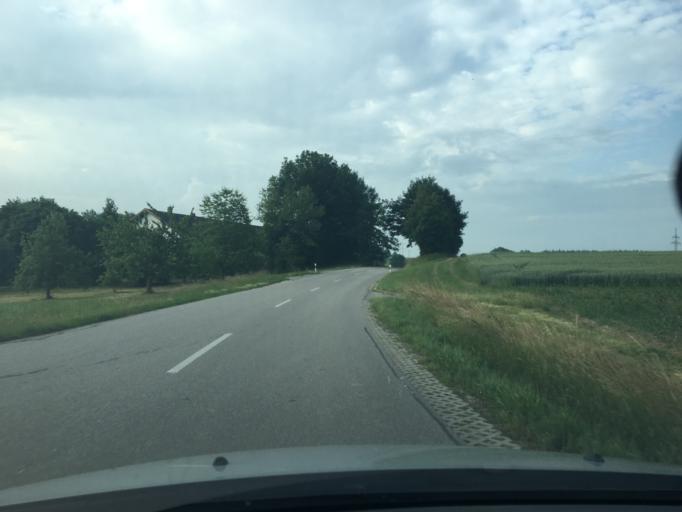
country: DE
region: Bavaria
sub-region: Lower Bavaria
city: Furth
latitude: 48.3969
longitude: 12.3548
